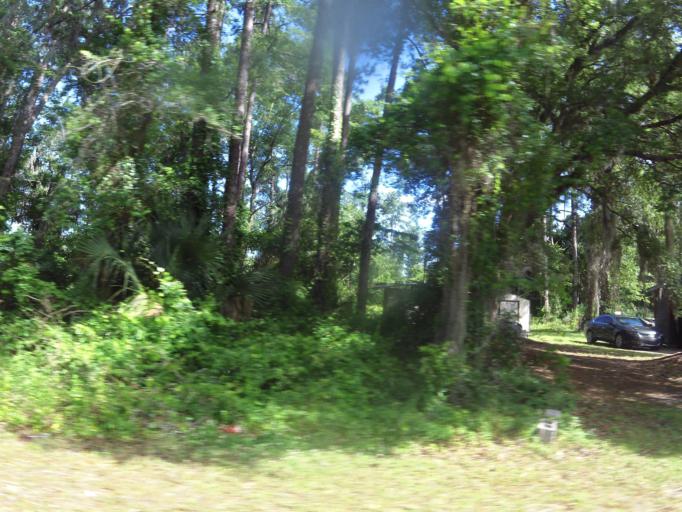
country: US
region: Florida
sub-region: Nassau County
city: Hilliard
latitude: 30.7002
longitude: -81.9295
